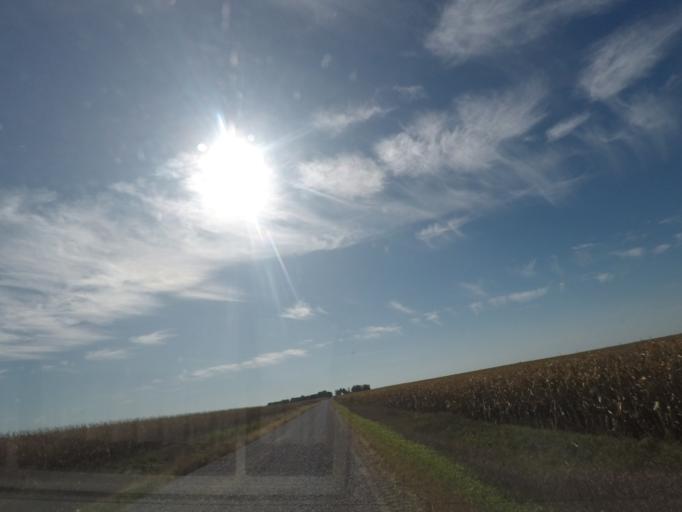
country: US
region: Iowa
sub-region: Story County
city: Nevada
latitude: 42.0597
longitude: -93.3290
